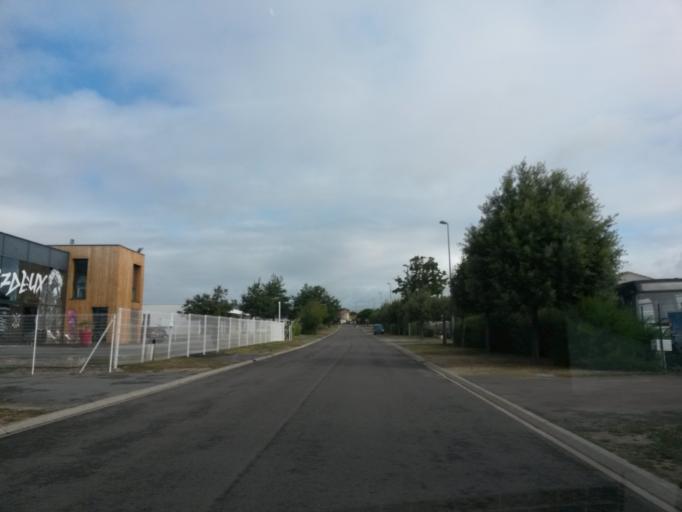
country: FR
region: Pays de la Loire
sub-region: Departement de la Vendee
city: Olonne-sur-Mer
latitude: 46.5211
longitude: -1.7847
